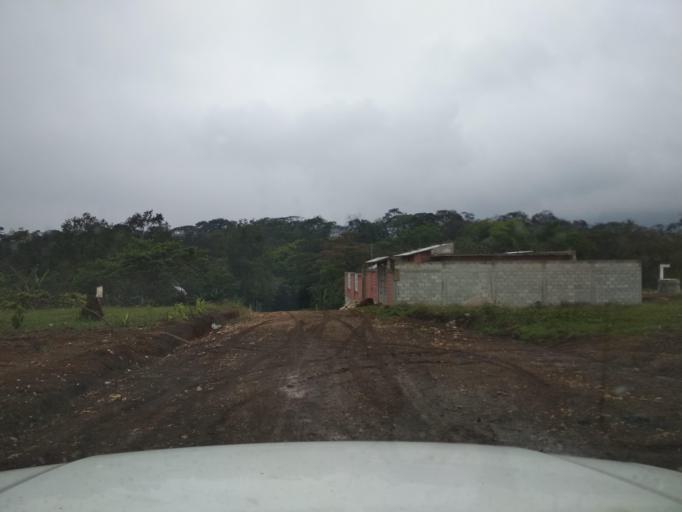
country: MX
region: Veracruz
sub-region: Cordoba
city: Fredepo
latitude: 18.8684
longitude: -96.9713
